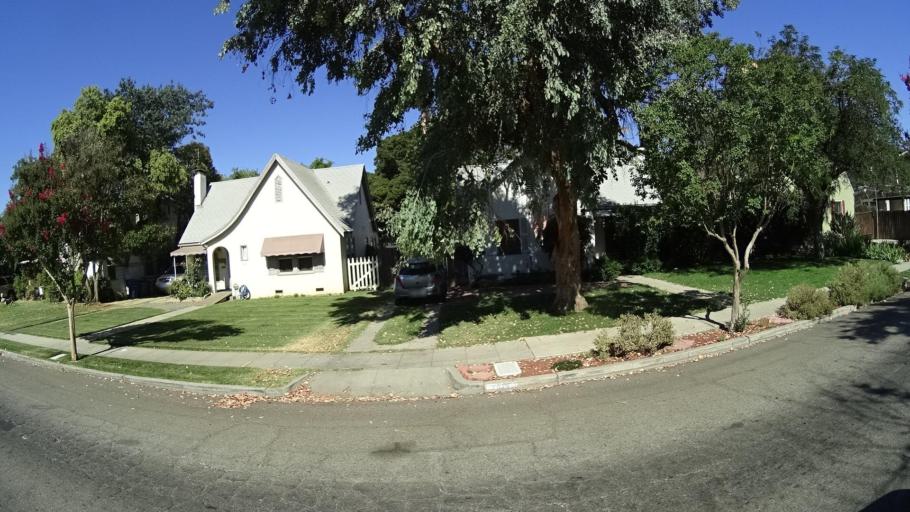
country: US
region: California
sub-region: Fresno County
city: Fresno
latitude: 36.7561
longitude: -119.7951
